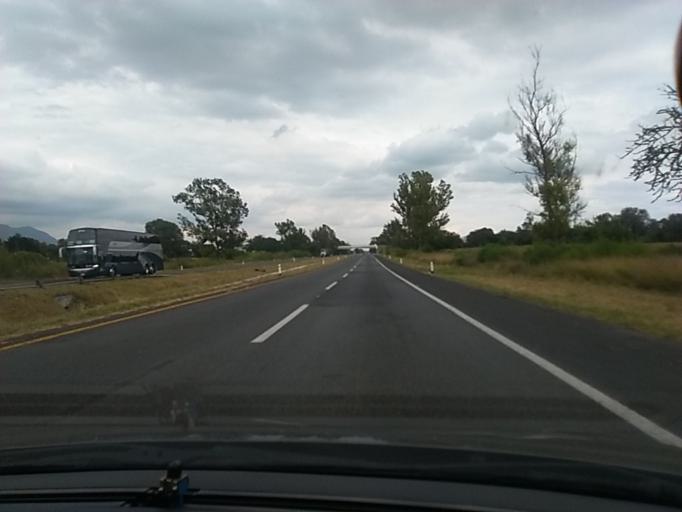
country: MX
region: Jalisco
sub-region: Ocotlan
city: Joconoxtle (La Tuna)
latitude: 20.3804
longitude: -102.6951
